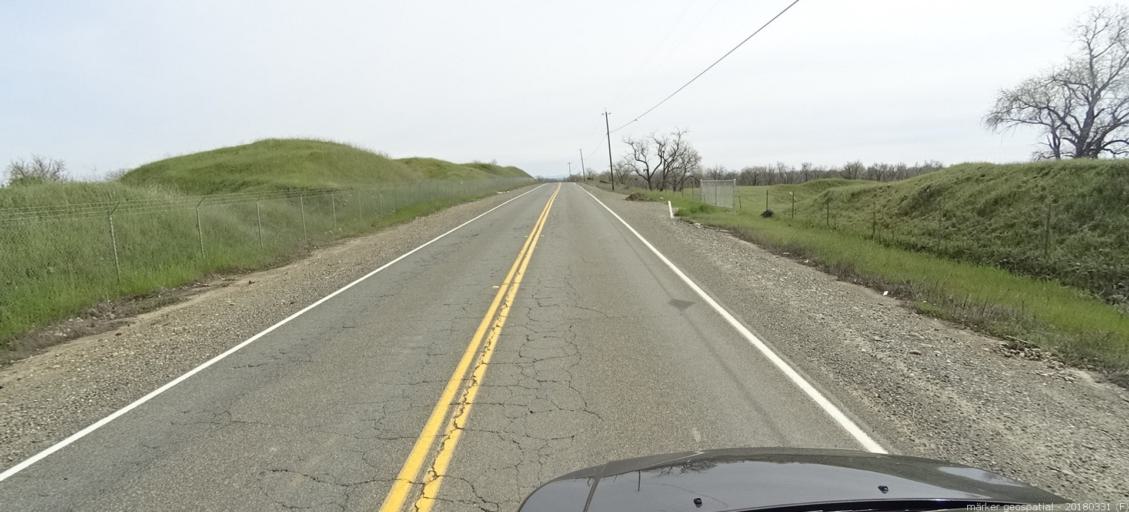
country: US
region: California
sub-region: Sacramento County
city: Gold River
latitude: 38.5936
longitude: -121.1979
